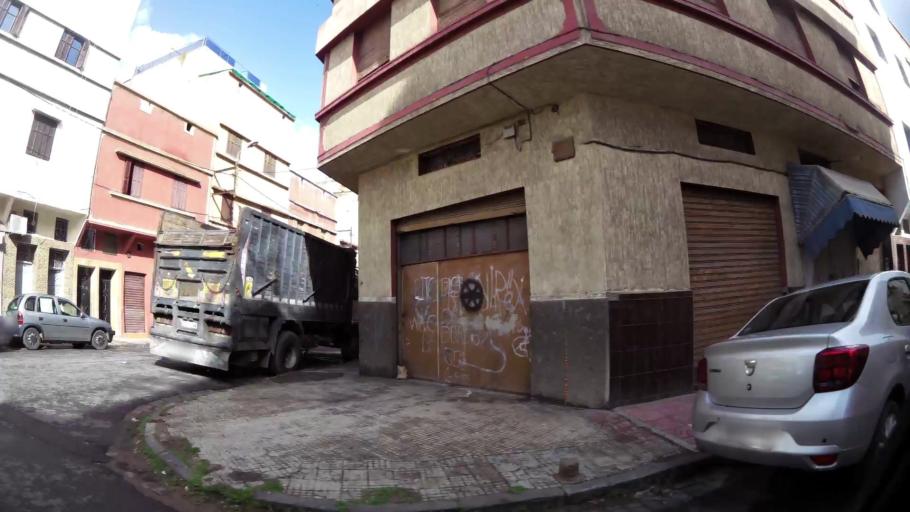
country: MA
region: Grand Casablanca
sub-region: Casablanca
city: Casablanca
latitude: 33.5717
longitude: -7.5817
